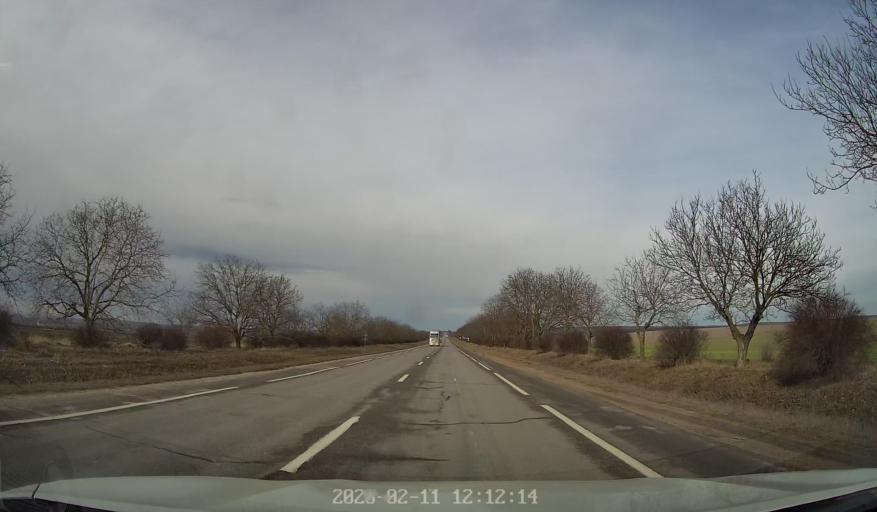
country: MD
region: Riscani
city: Riscani
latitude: 48.0618
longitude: 27.5070
